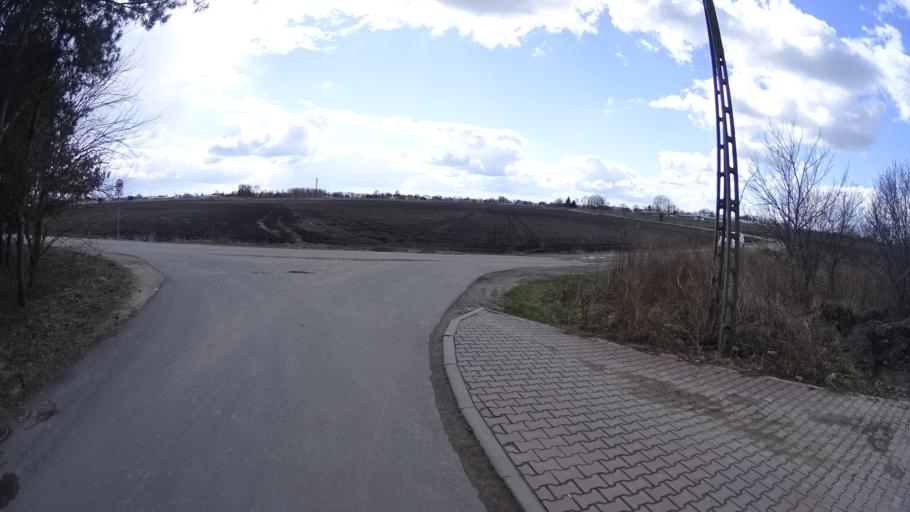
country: PL
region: Masovian Voivodeship
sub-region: Powiat warszawski zachodni
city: Jozefow
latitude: 52.2242
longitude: 20.7261
